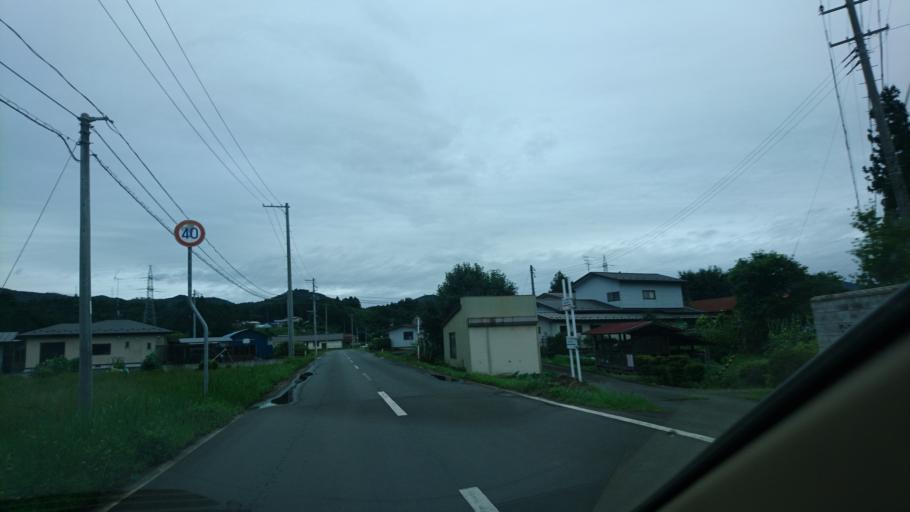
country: JP
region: Iwate
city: Mizusawa
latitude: 39.0724
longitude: 141.1816
